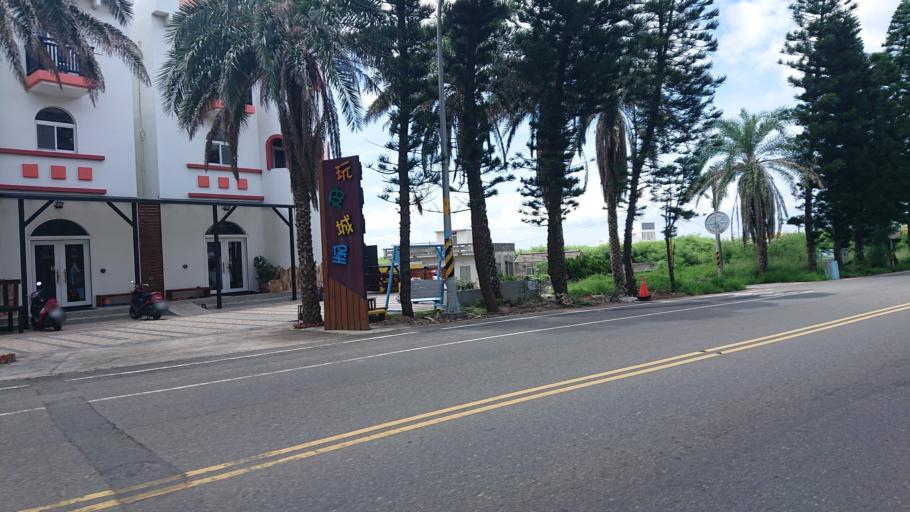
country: TW
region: Taiwan
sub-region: Penghu
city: Ma-kung
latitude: 23.5830
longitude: 119.6070
